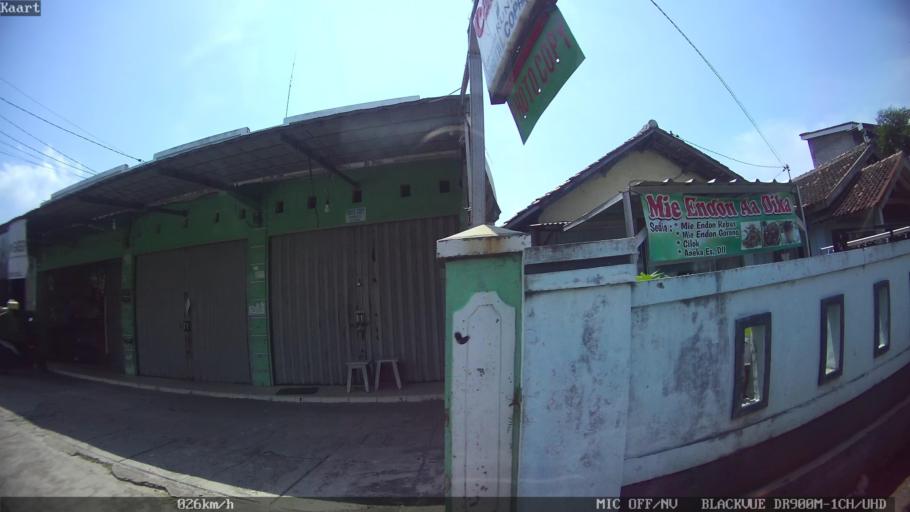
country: ID
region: Lampung
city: Kedaton
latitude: -5.3972
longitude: 105.2653
